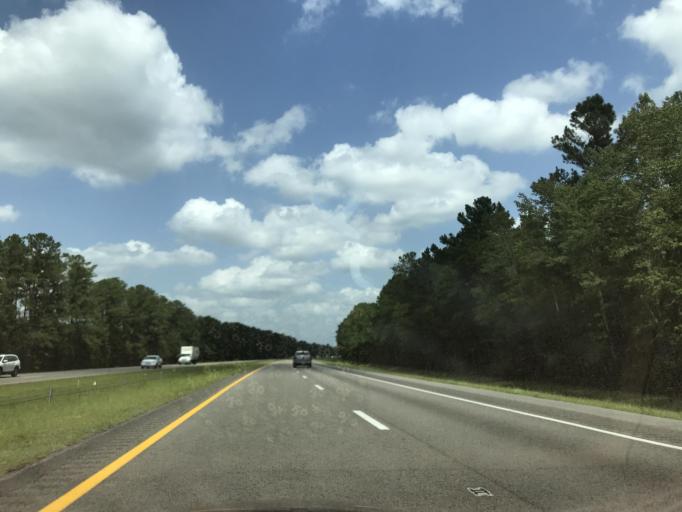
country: US
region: North Carolina
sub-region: Pender County
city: Burgaw
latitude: 34.5320
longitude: -77.8927
